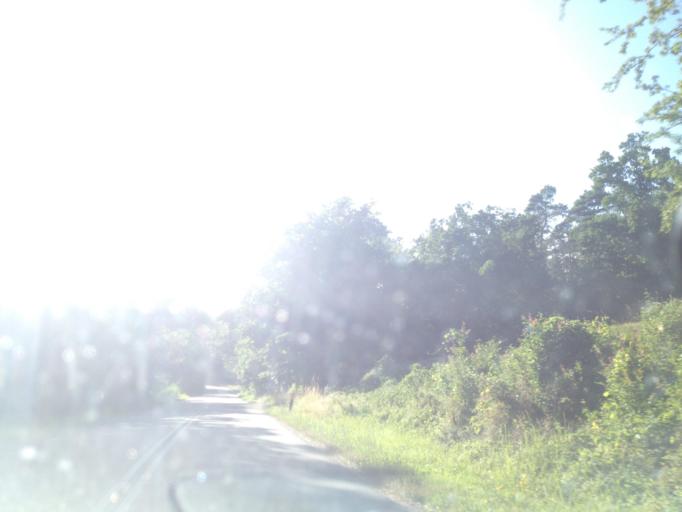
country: DK
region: Capital Region
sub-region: Halsnaes Kommune
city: Frederiksvaerk
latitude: 56.0290
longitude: 12.0913
